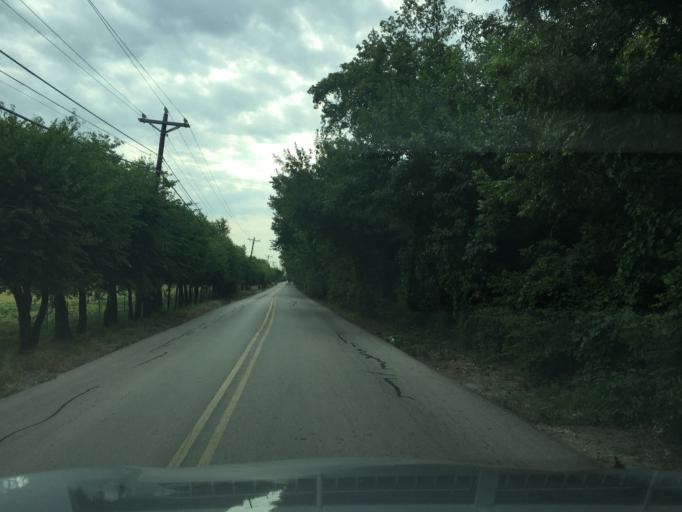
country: US
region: Texas
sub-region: Collin County
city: Saint Paul
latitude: 33.0313
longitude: -96.5791
